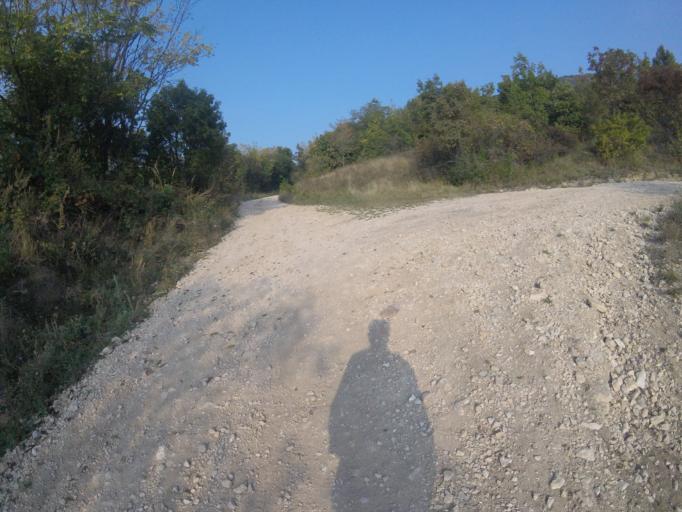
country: HU
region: Pest
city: Pilisszanto
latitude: 47.6761
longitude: 18.8776
